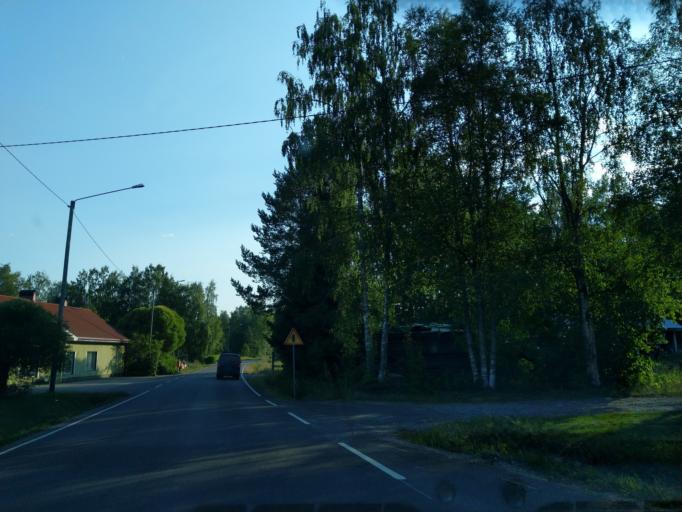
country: FI
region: Satakunta
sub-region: Pohjois-Satakunta
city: Honkajoki
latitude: 61.8220
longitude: 22.2023
